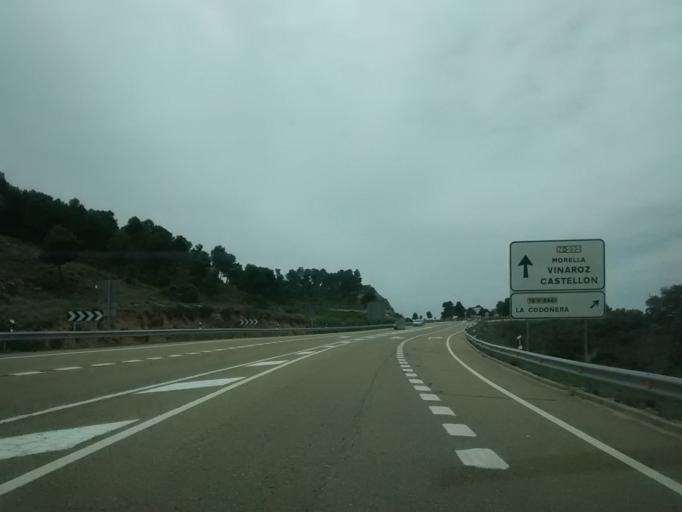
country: ES
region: Aragon
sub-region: Provincia de Teruel
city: Fornoles
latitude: 40.9142
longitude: -0.0212
